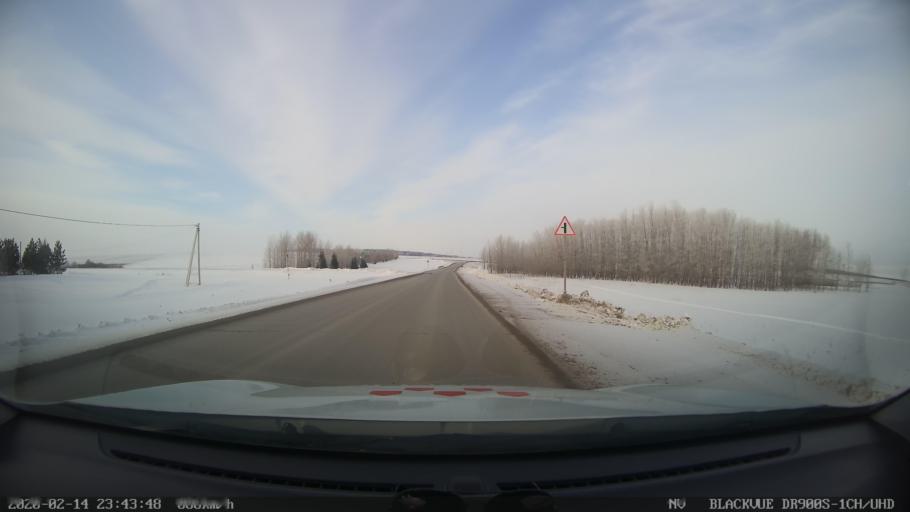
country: RU
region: Tatarstan
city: Kuybyshevskiy Zaton
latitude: 55.2062
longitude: 49.2482
